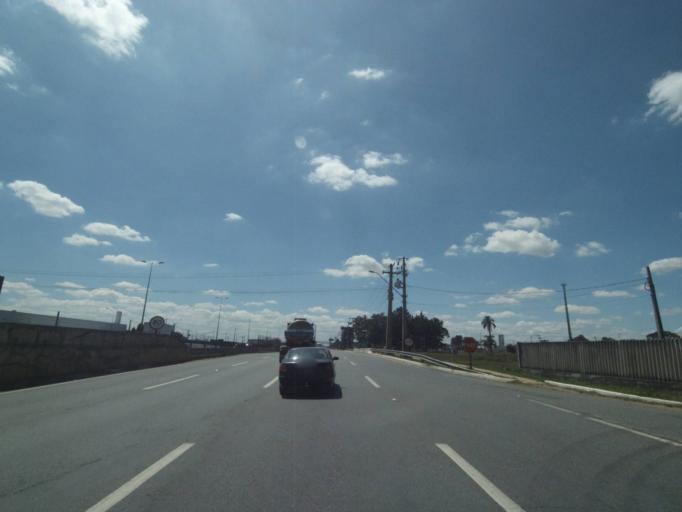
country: BR
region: Parana
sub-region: Sao Jose Dos Pinhais
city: Sao Jose dos Pinhais
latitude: -25.5555
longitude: -49.3057
